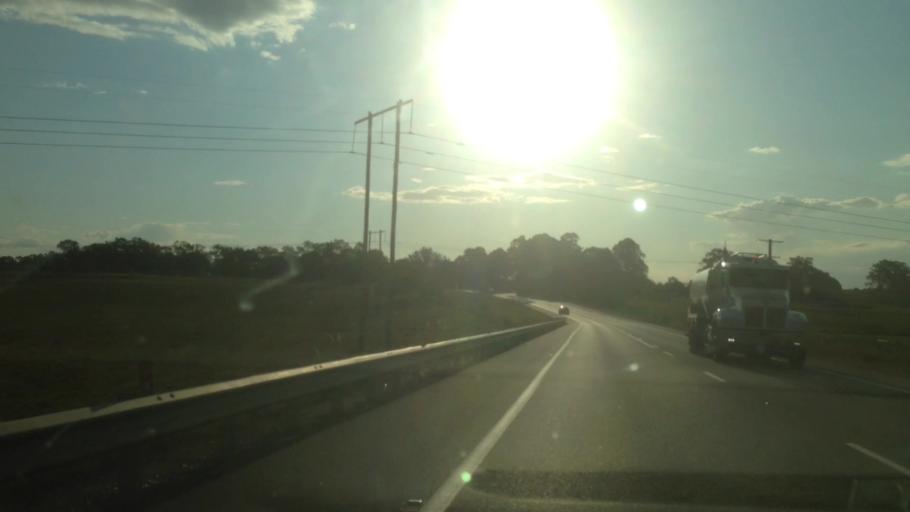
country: AU
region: New South Wales
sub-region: Cessnock
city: Heddon Greta
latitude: -32.8310
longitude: 151.5190
